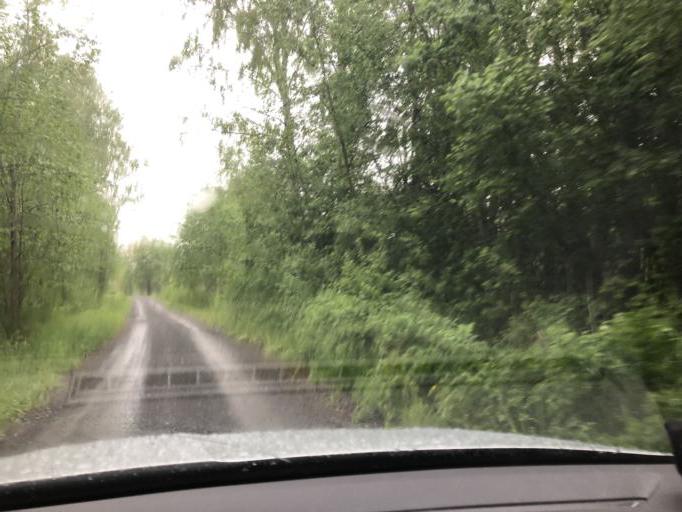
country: SE
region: Vaesternorrland
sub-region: Haernoesands Kommun
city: Haernoesand
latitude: 62.7932
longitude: 17.9258
